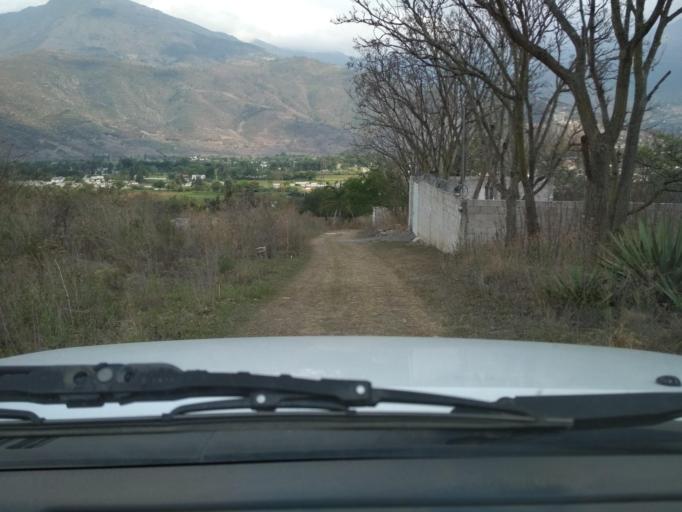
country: MX
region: Veracruz
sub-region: Acultzingo
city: Acatla
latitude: 18.7730
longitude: -97.2283
